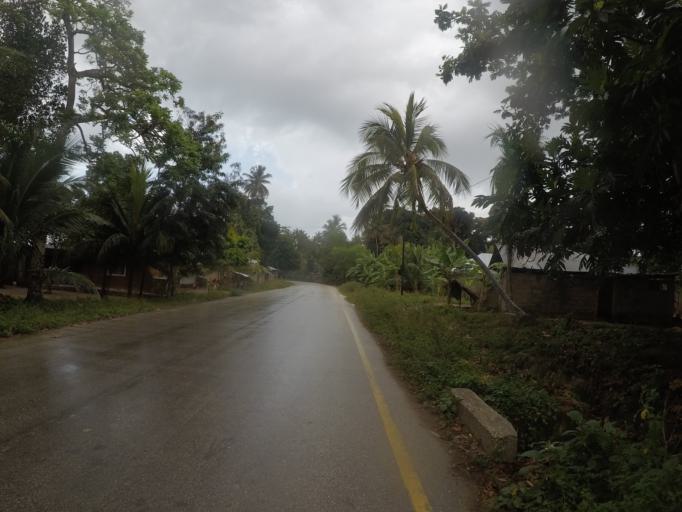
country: TZ
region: Zanzibar North
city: Mkokotoni
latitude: -5.9673
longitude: 39.1967
